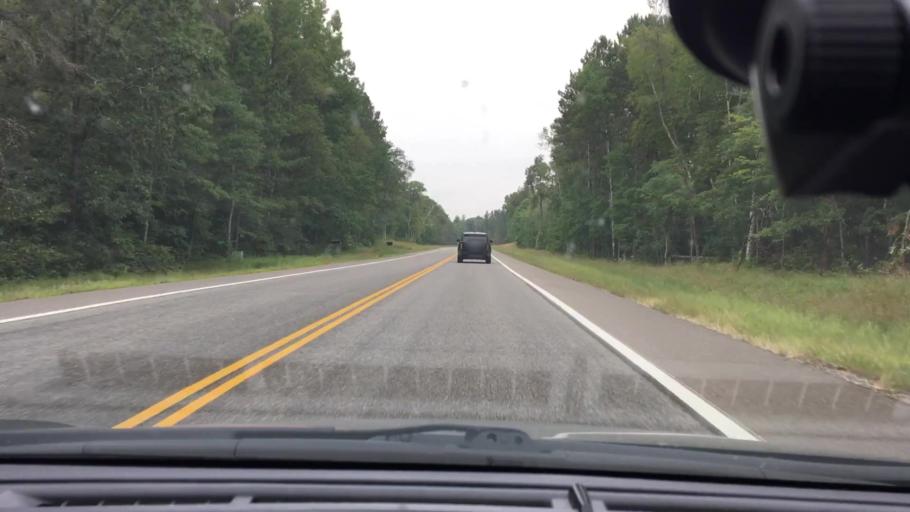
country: US
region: Minnesota
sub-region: Crow Wing County
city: Cross Lake
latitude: 46.6617
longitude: -94.0354
